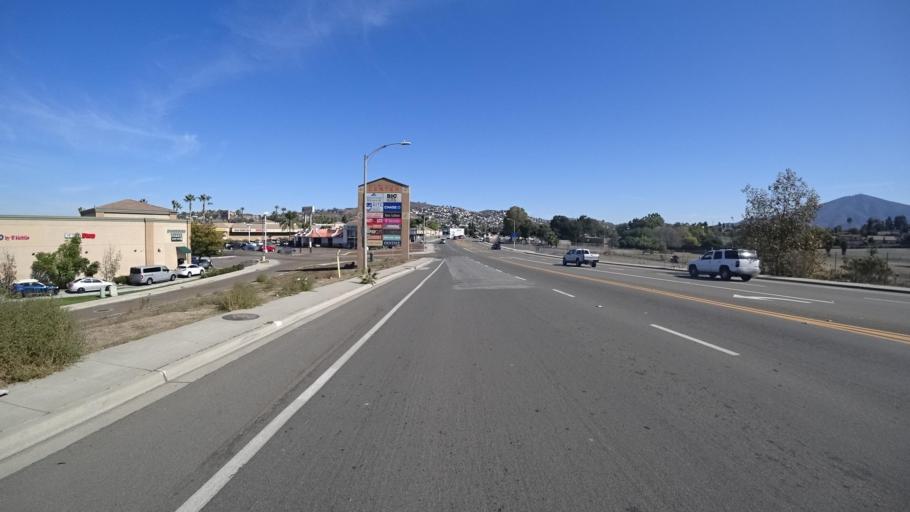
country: US
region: California
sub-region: San Diego County
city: La Presa
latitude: 32.7060
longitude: -117.0095
